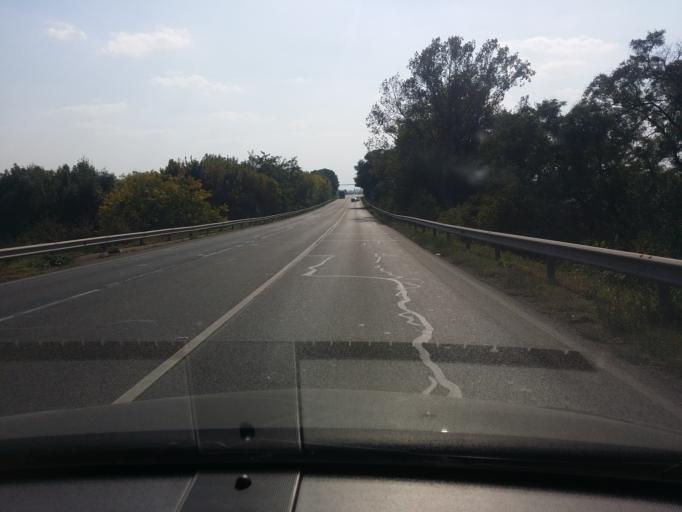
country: HU
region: Fejer
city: Baracs
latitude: 46.9197
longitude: 18.9292
